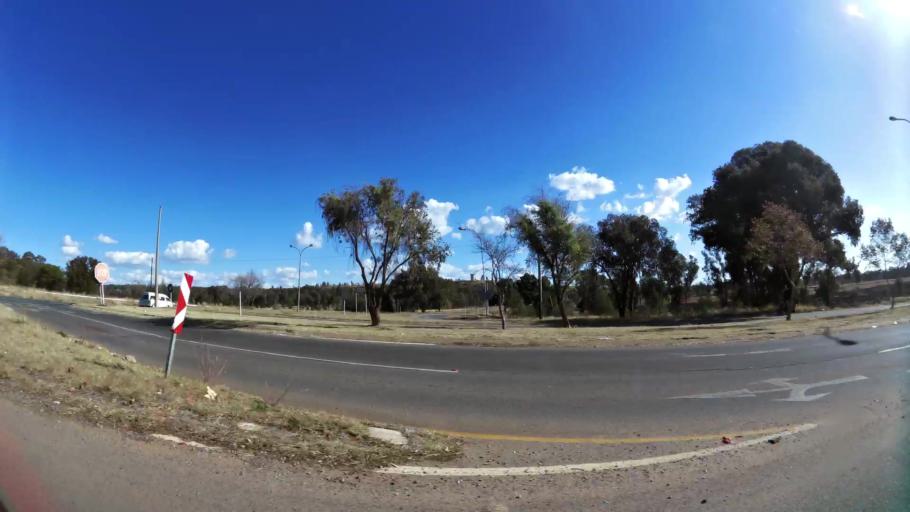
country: ZA
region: Gauteng
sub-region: West Rand District Municipality
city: Carletonville
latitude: -26.3759
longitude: 27.3980
